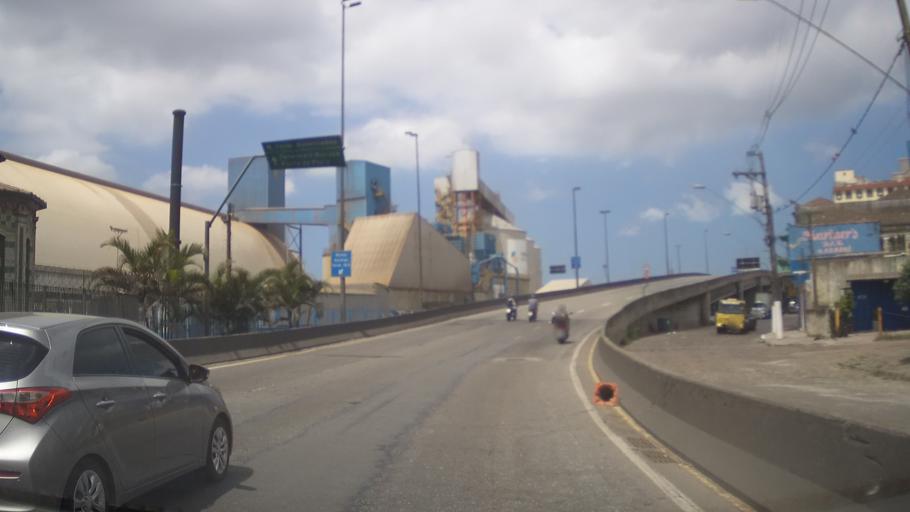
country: BR
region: Sao Paulo
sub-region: Santos
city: Santos
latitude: -23.9354
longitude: -46.3156
